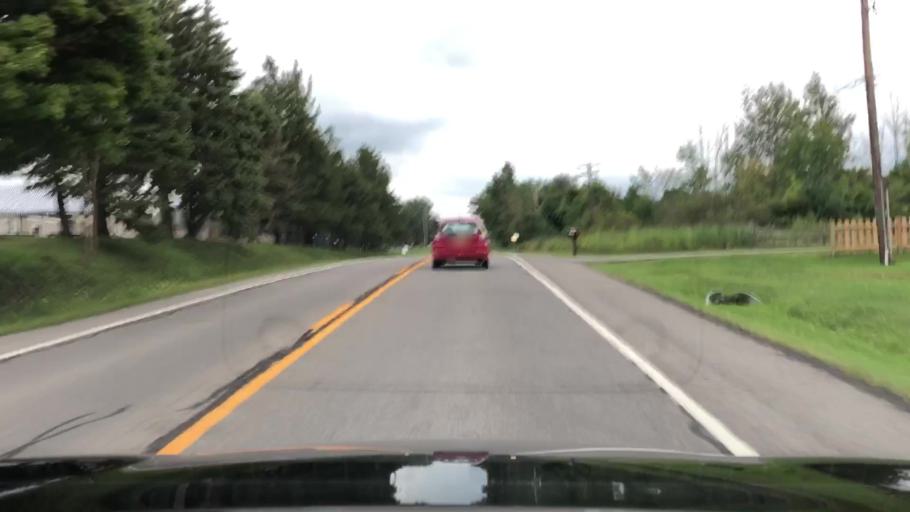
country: US
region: New York
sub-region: Erie County
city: Orchard Park
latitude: 42.7727
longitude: -78.6968
